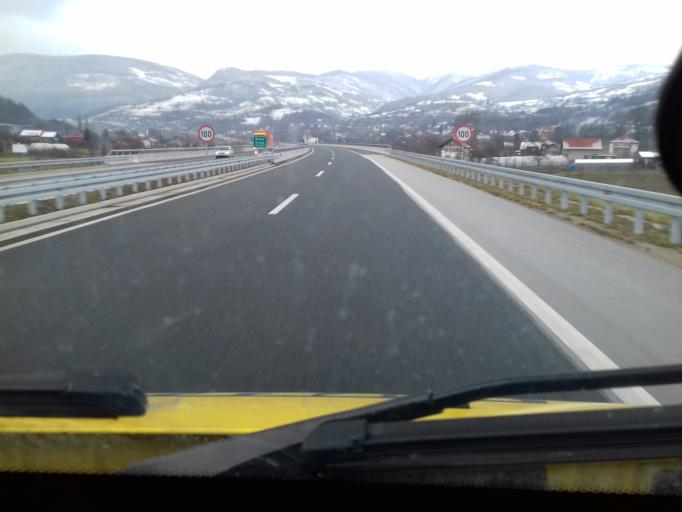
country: BA
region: Federation of Bosnia and Herzegovina
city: Zenica
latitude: 44.1656
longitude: 17.9700
